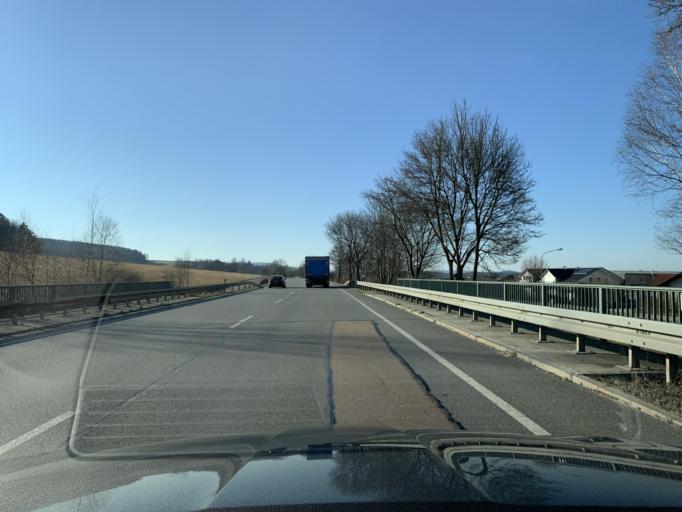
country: DE
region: Bavaria
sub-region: Upper Palatinate
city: Schonthal
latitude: 49.3303
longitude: 12.6255
